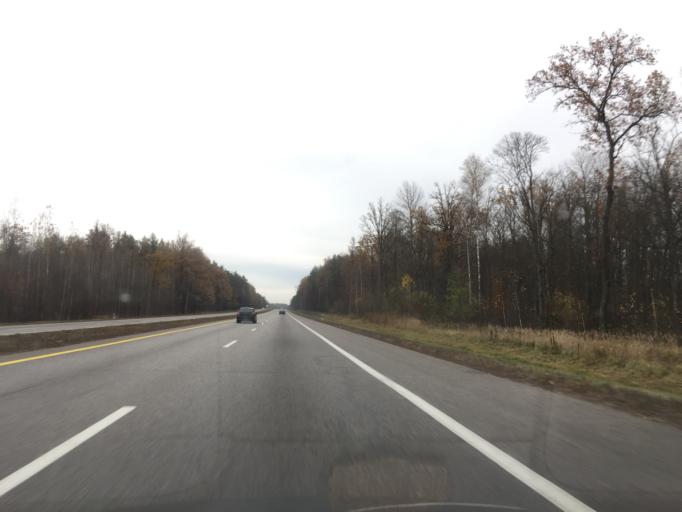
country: BY
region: Gomel
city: Gomel
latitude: 52.3621
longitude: 30.7307
